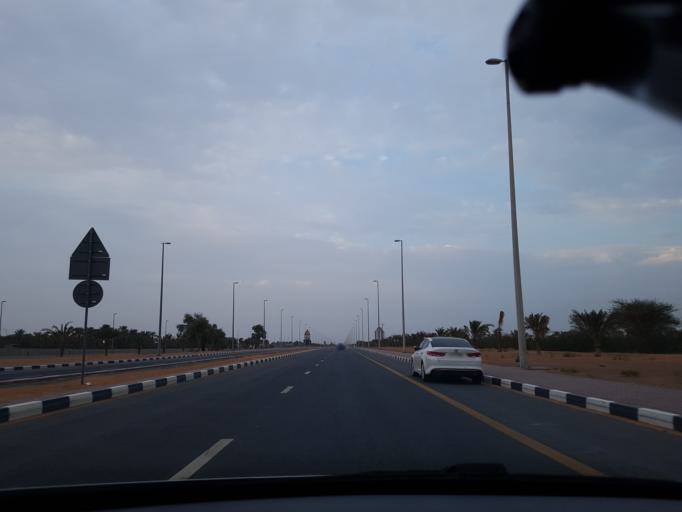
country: AE
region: Ash Shariqah
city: Adh Dhayd
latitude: 25.2692
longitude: 55.9118
